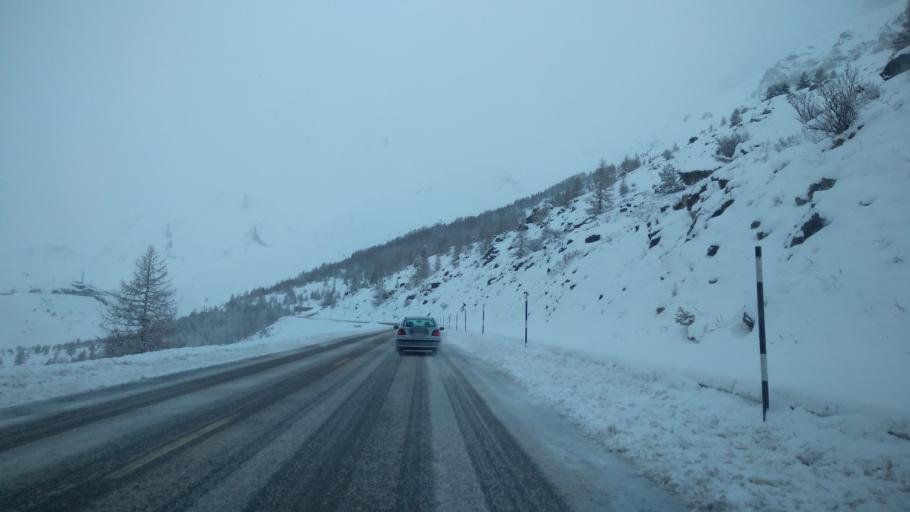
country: FR
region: Provence-Alpes-Cote d'Azur
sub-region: Departement des Hautes-Alpes
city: Le Monetier-les-Bains
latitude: 45.0343
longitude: 6.4383
